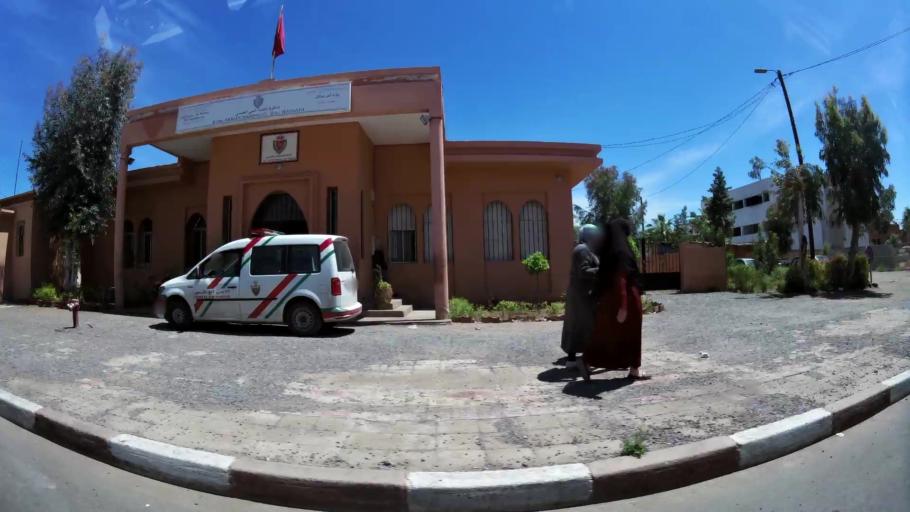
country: MA
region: Marrakech-Tensift-Al Haouz
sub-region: Marrakech
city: Marrakesh
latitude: 31.6321
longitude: -8.0453
